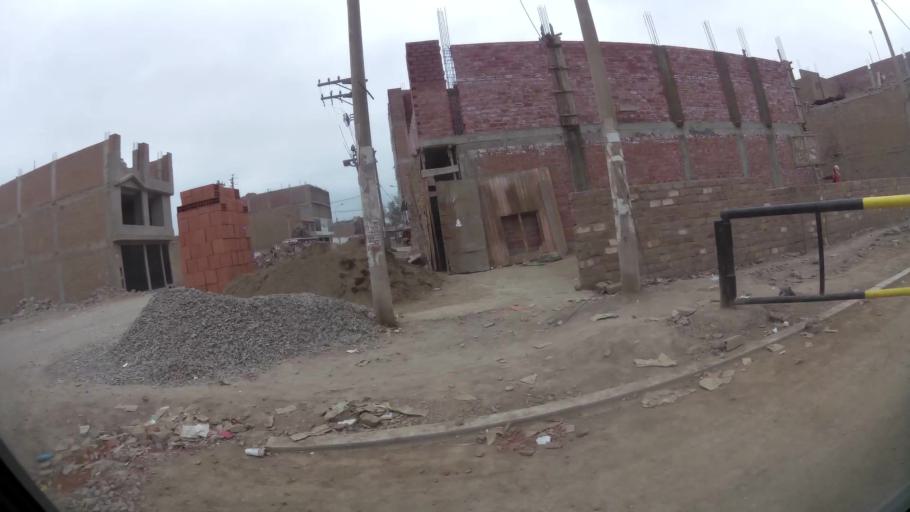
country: PE
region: Lima
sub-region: Lima
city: Independencia
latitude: -11.9565
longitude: -77.0924
